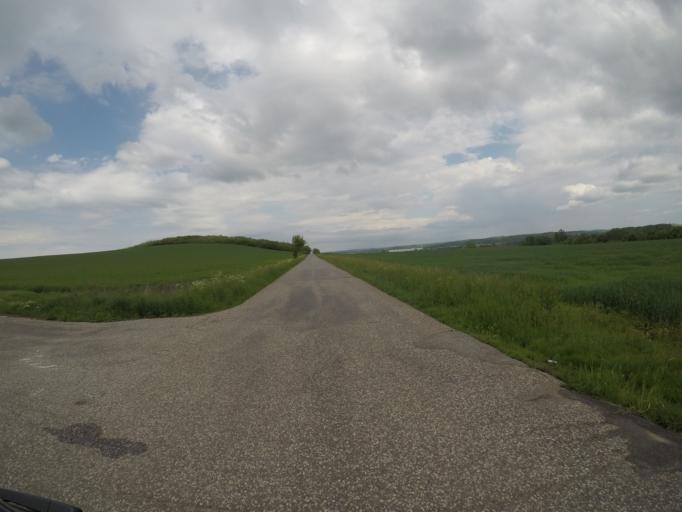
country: SK
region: Nitriansky
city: Sahy
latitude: 48.0816
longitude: 18.8653
